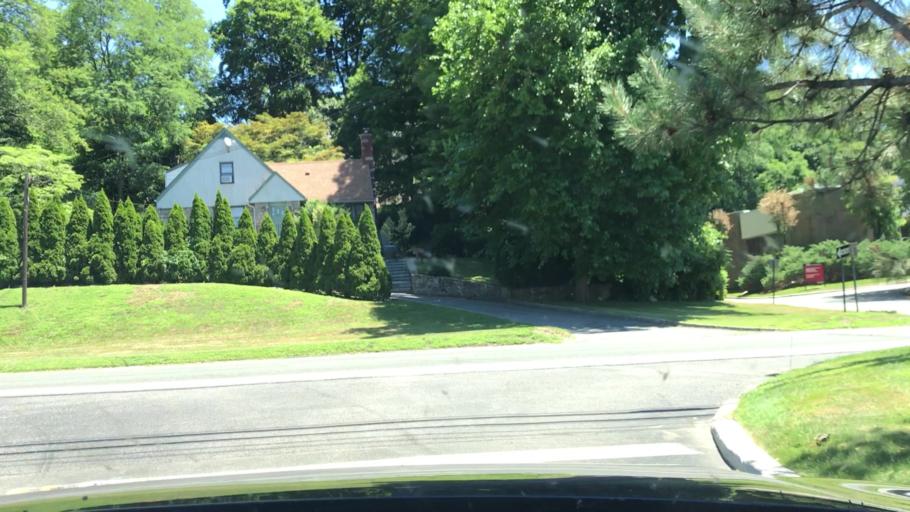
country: US
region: New York
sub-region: Westchester County
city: Hawthorne
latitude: 41.1021
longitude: -73.8082
